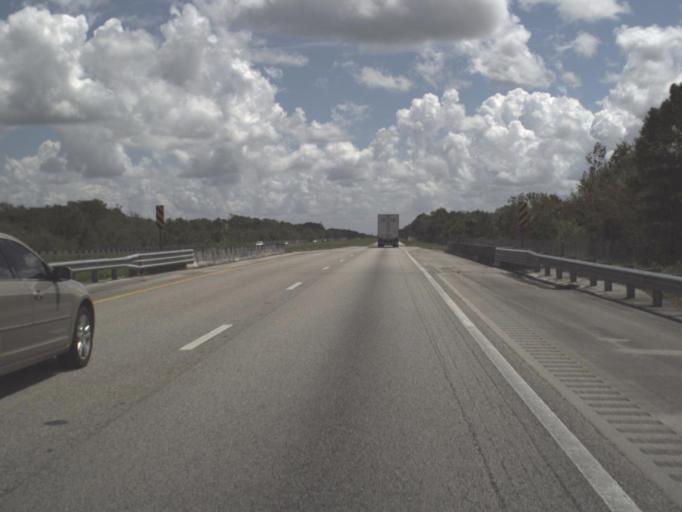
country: US
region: Florida
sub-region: Collier County
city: Orangetree
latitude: 26.1534
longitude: -81.4326
